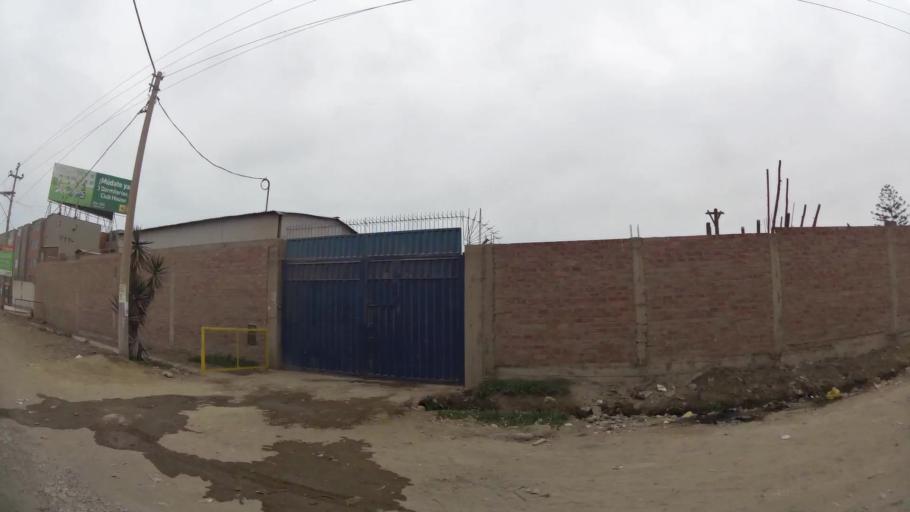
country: PE
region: Lima
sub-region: Lima
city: Surco
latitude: -12.2086
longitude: -76.9677
